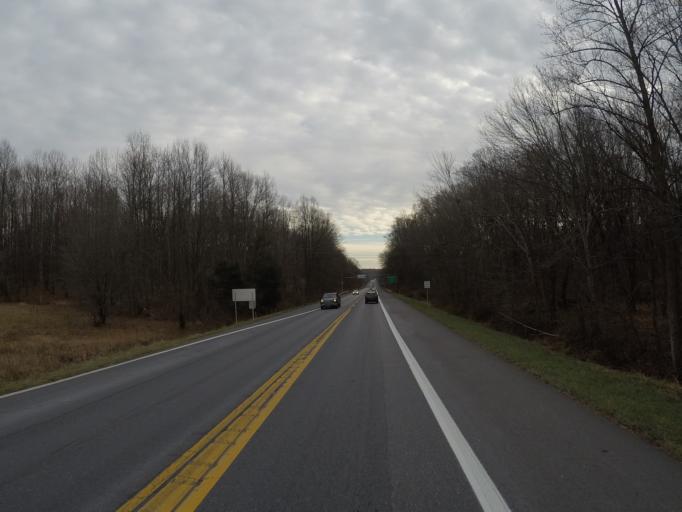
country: US
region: Maryland
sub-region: Howard County
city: Highland
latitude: 39.2485
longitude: -76.9786
